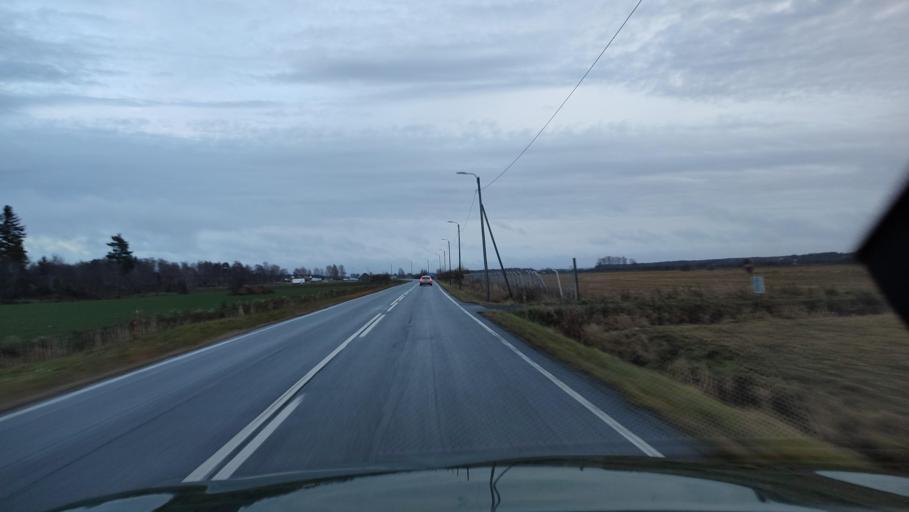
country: FI
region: Ostrobothnia
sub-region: Vaasa
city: Ristinummi
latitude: 63.0458
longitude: 21.7461
